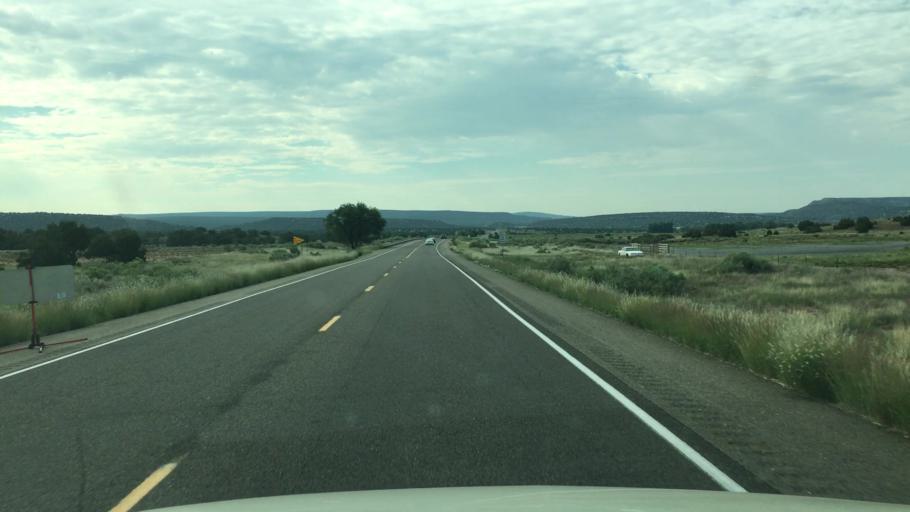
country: US
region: New Mexico
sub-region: Santa Fe County
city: Eldorado at Santa Fe
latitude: 35.4148
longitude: -105.8689
